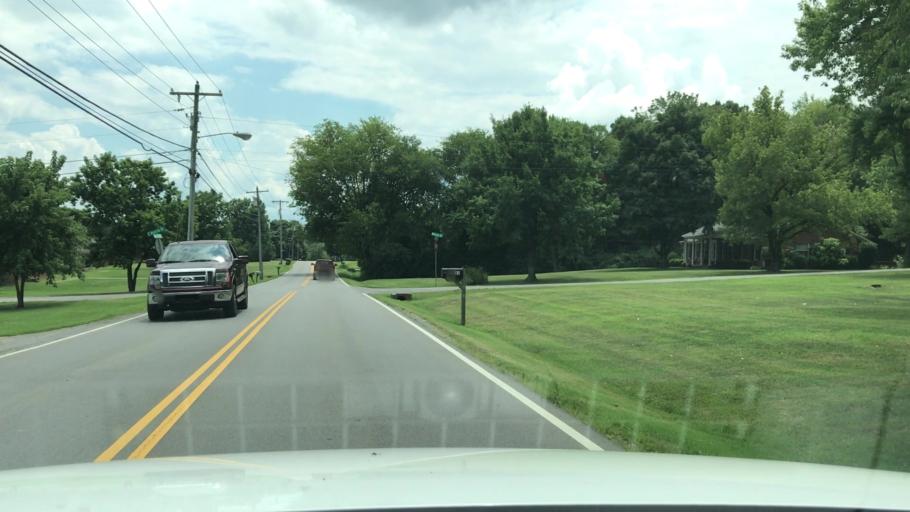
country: US
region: Tennessee
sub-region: Sumner County
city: Gallatin
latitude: 36.3703
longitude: -86.4674
